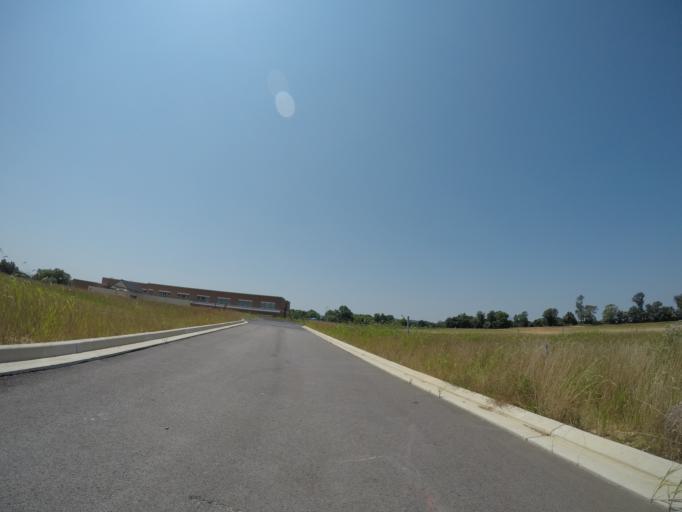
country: US
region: Maryland
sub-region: Frederick County
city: Urbana
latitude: 39.3286
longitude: -77.3660
